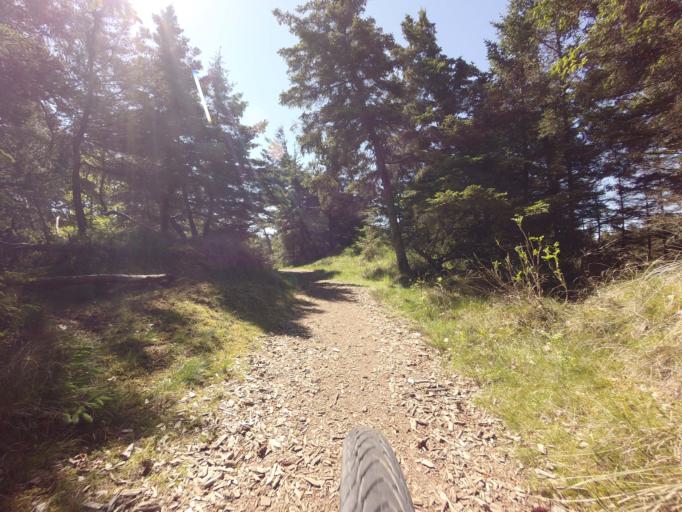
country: DK
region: North Denmark
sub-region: Jammerbugt Kommune
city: Pandrup
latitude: 57.3020
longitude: 9.6511
